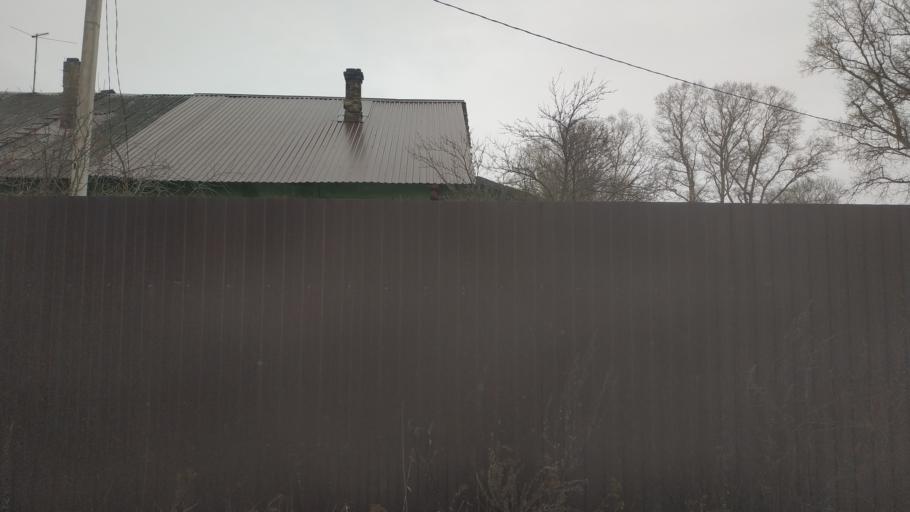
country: RU
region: Tverskaya
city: Tver
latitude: 56.8950
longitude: 35.8470
